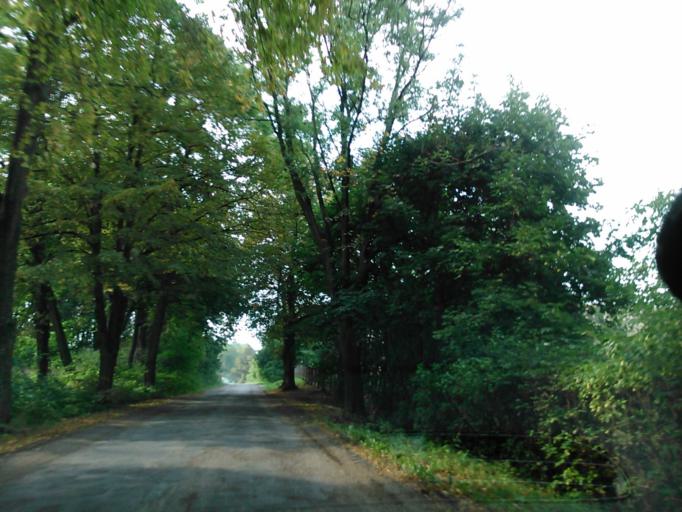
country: PL
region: Kujawsko-Pomorskie
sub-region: Powiat wabrzeski
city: Pluznica
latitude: 53.2350
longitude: 18.8230
